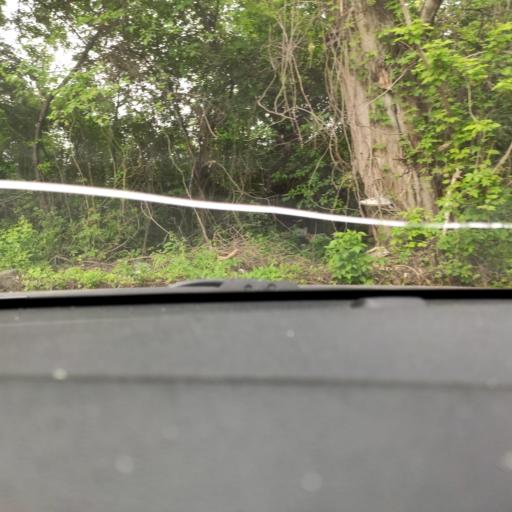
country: RU
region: Voronezj
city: Voronezh
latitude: 51.5942
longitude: 39.1654
